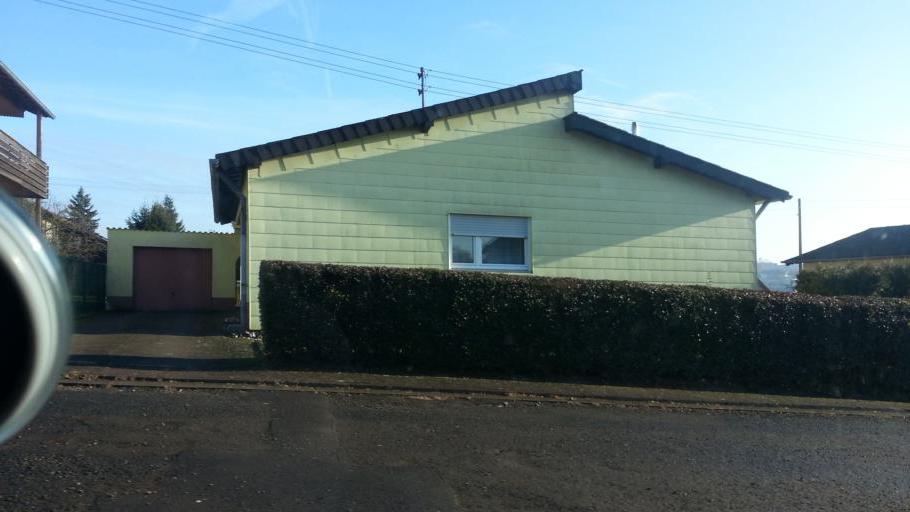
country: DE
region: Saarland
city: Tholey
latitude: 49.4777
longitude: 7.0276
